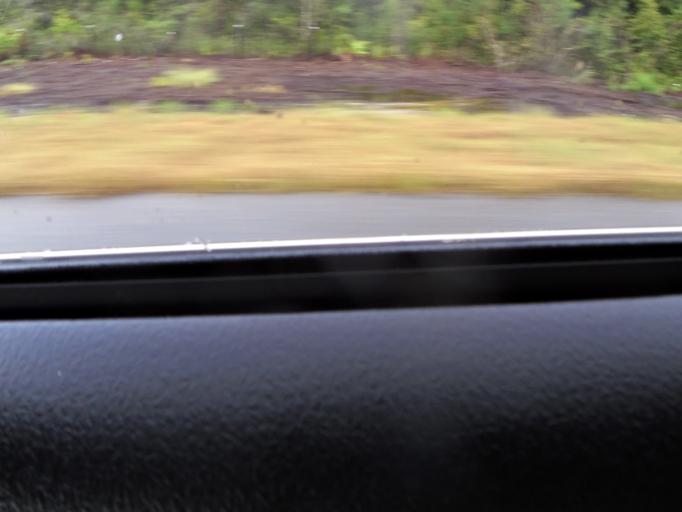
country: US
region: Georgia
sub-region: Wayne County
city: Jesup
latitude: 31.6149
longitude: -81.8616
